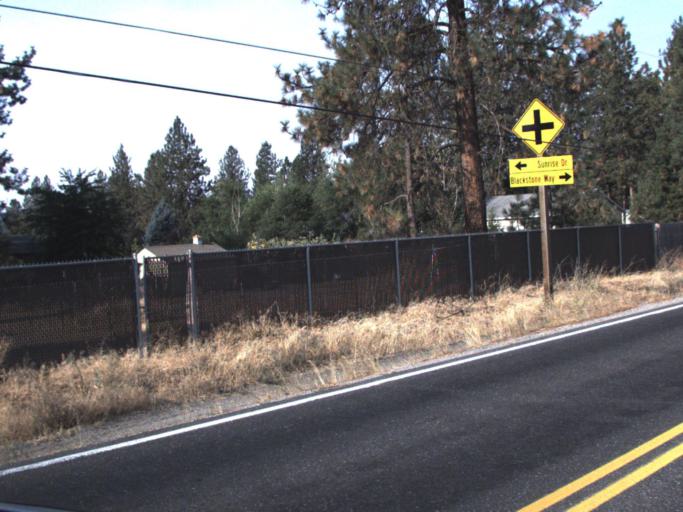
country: US
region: Washington
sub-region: Spokane County
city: Fairwood
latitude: 47.8119
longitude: -117.5673
